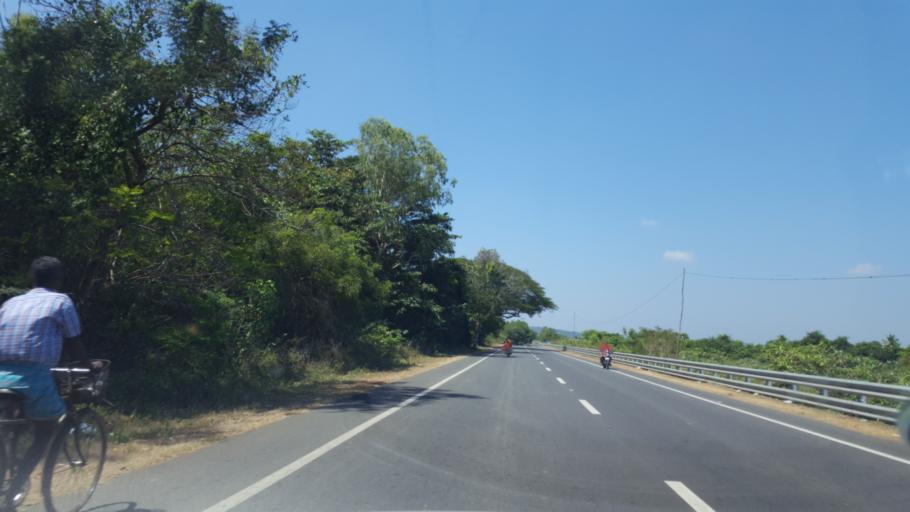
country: IN
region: Tamil Nadu
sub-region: Kancheepuram
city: Karumbakkam
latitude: 12.6289
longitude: 80.0507
